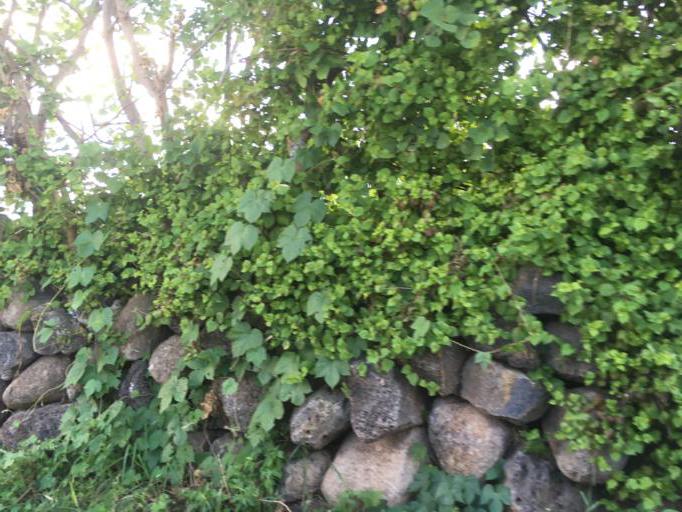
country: MX
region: Michoacan
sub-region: Morelia
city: Villa Magna
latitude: 19.6515
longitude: -101.3195
